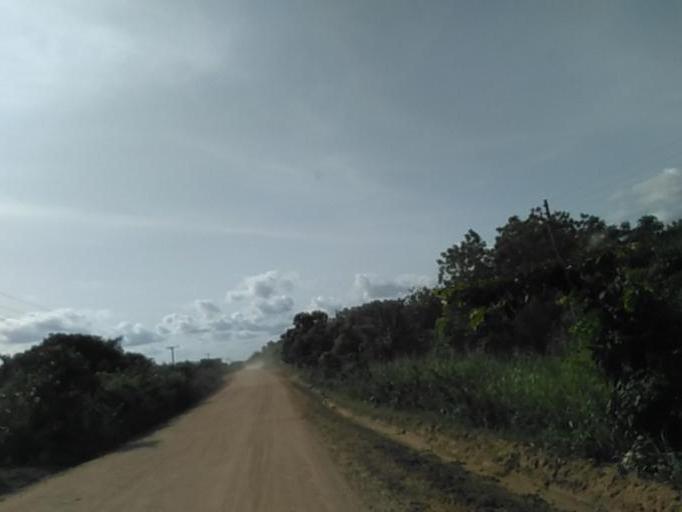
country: GH
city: Akropong
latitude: 6.0484
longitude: 0.2968
